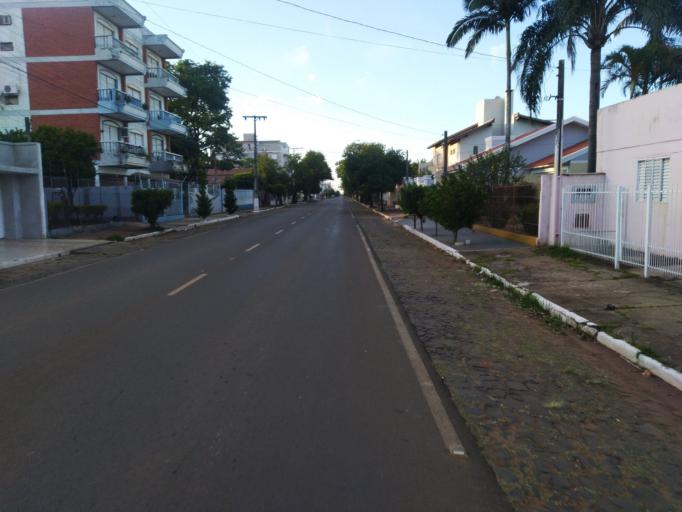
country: BR
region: Rio Grande do Sul
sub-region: Sao Borja
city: Sao Borja
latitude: -28.6587
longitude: -56.0094
